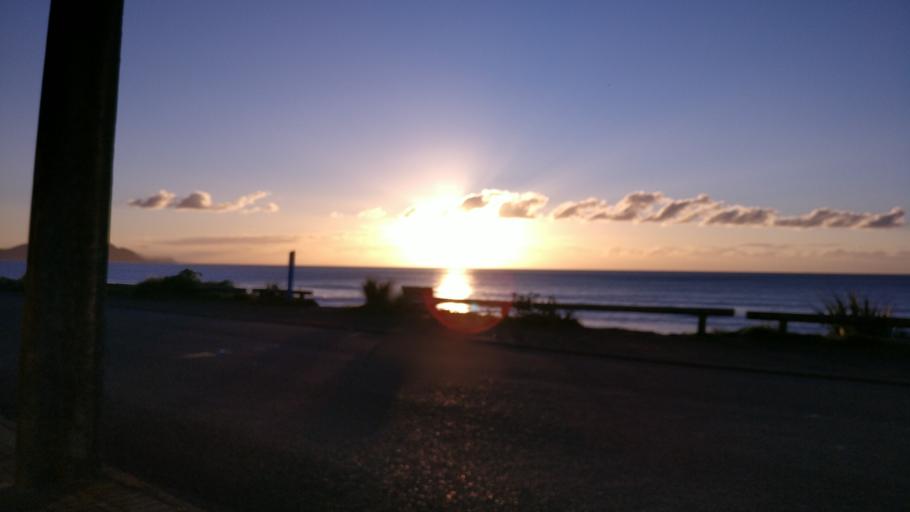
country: NZ
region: Wellington
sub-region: Kapiti Coast District
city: Paraparaumu
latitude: -40.9804
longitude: 174.9550
